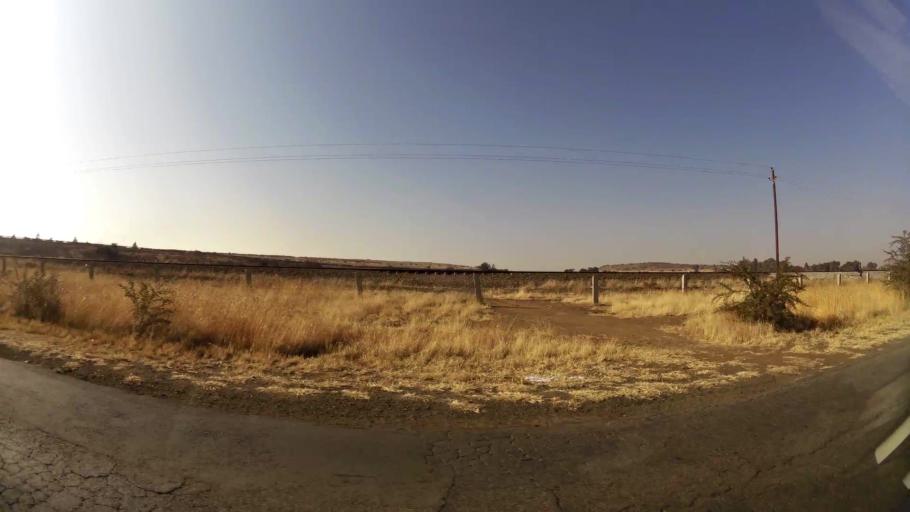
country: ZA
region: Orange Free State
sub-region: Mangaung Metropolitan Municipality
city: Bloemfontein
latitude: -29.1826
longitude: 26.1883
